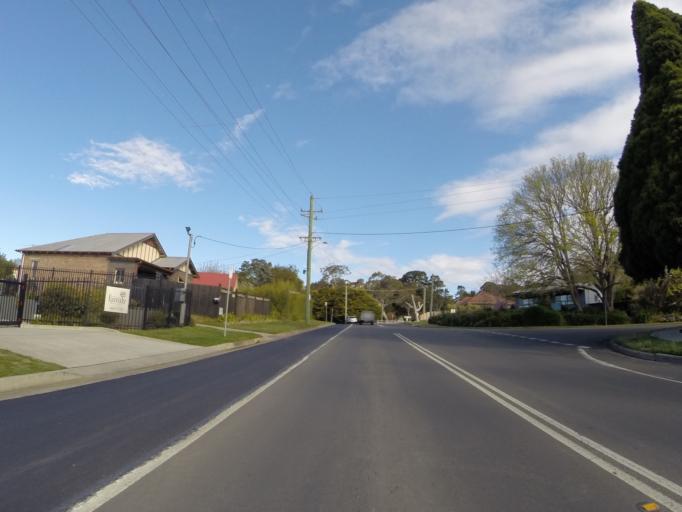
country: AU
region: New South Wales
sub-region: Wingecarribee
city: Moss Vale
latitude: -34.5469
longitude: 150.3801
